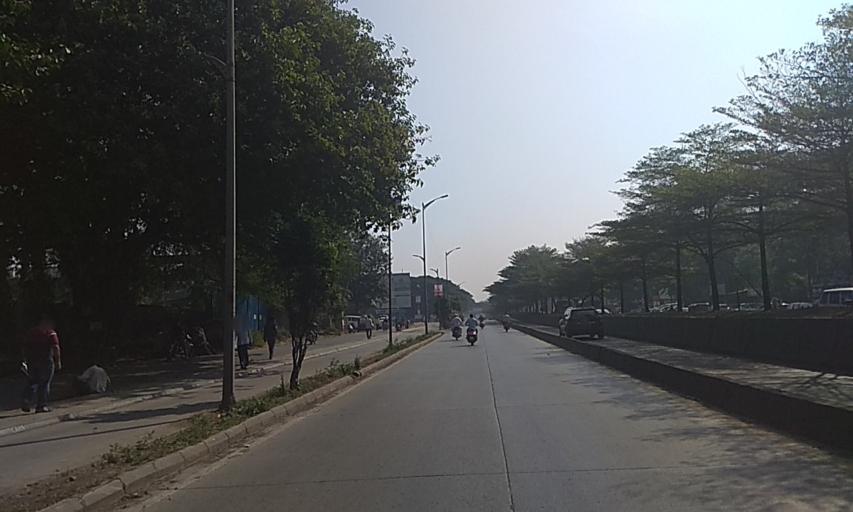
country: IN
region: Maharashtra
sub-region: Pune Division
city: Pune
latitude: 18.5036
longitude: 73.9234
